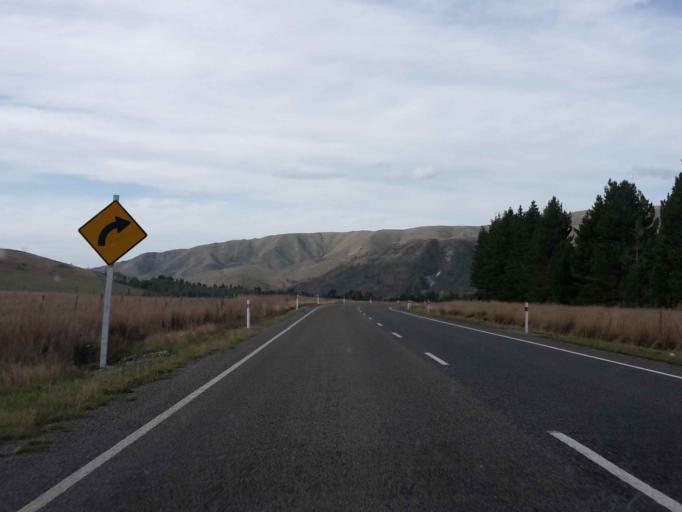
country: NZ
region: Canterbury
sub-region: Timaru District
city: Pleasant Point
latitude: -44.0898
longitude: 170.6348
